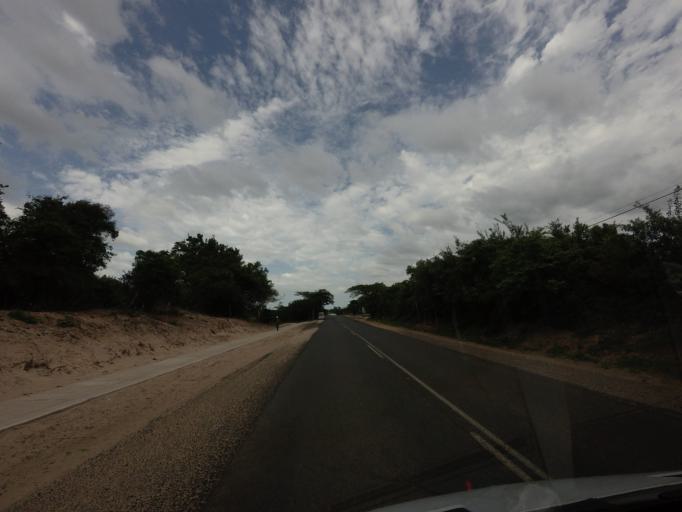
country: ZA
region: KwaZulu-Natal
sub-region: uMkhanyakude District Municipality
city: Mtubatuba
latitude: -28.3789
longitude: 32.3671
